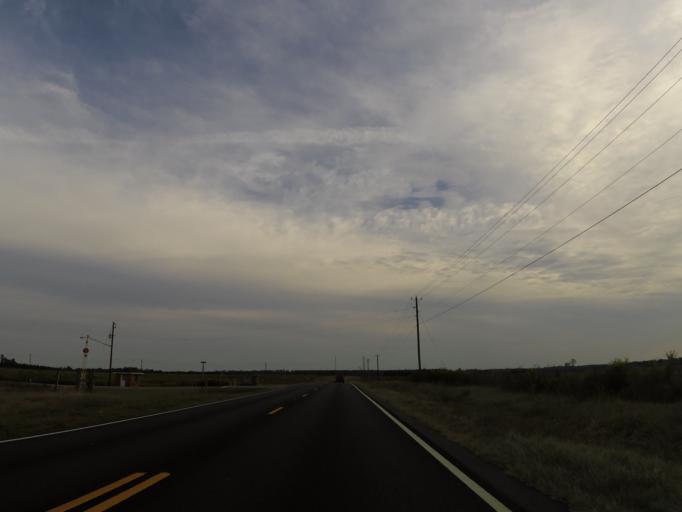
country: US
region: Alabama
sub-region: Escambia County
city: Atmore
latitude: 31.1387
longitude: -87.4636
